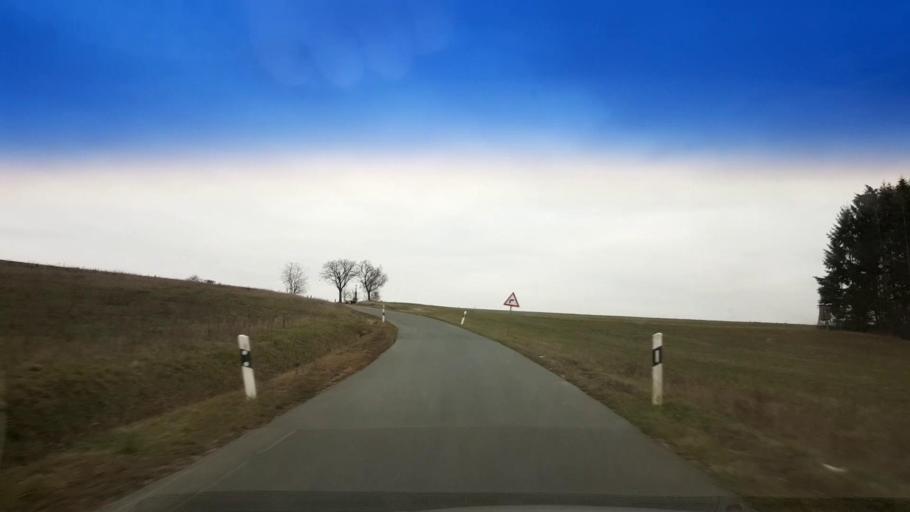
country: DE
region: Bavaria
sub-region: Upper Franconia
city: Pettstadt
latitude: 49.7872
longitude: 10.9139
